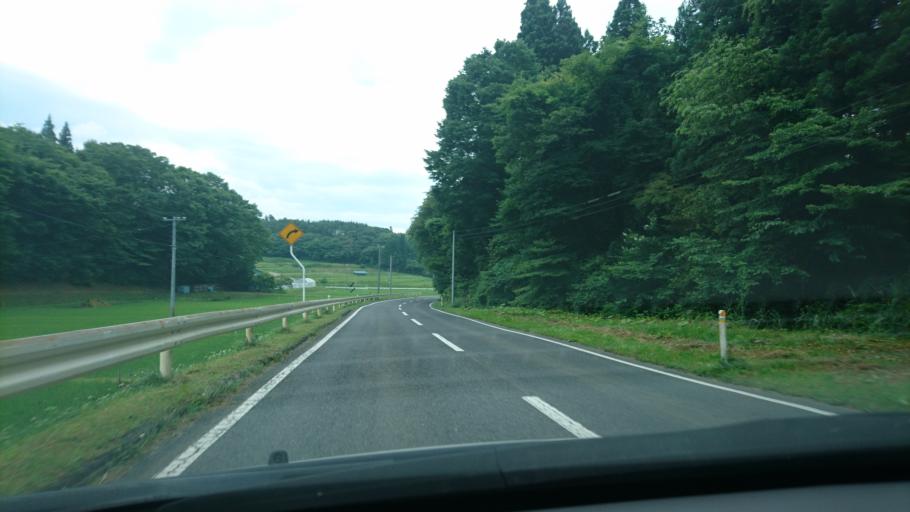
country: JP
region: Iwate
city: Ichinoseki
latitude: 38.8803
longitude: 141.4265
